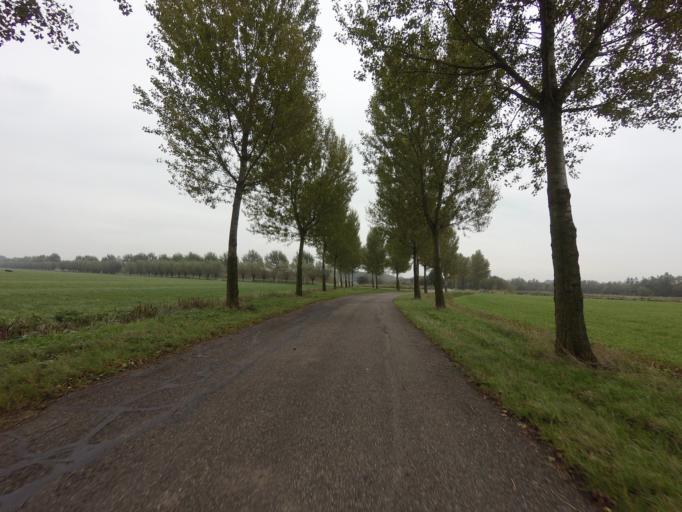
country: NL
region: Gelderland
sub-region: Gemeente Culemborg
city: Culemborg
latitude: 51.9302
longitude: 5.1743
